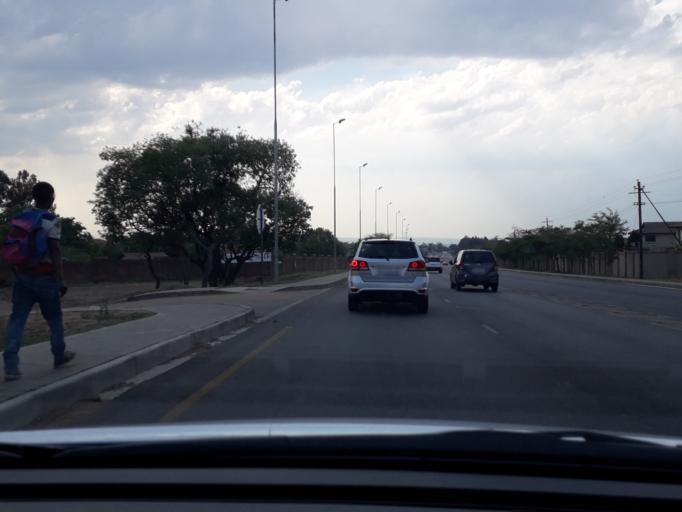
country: ZA
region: Gauteng
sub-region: City of Johannesburg Metropolitan Municipality
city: Diepsloot
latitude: -26.0082
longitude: 27.9912
